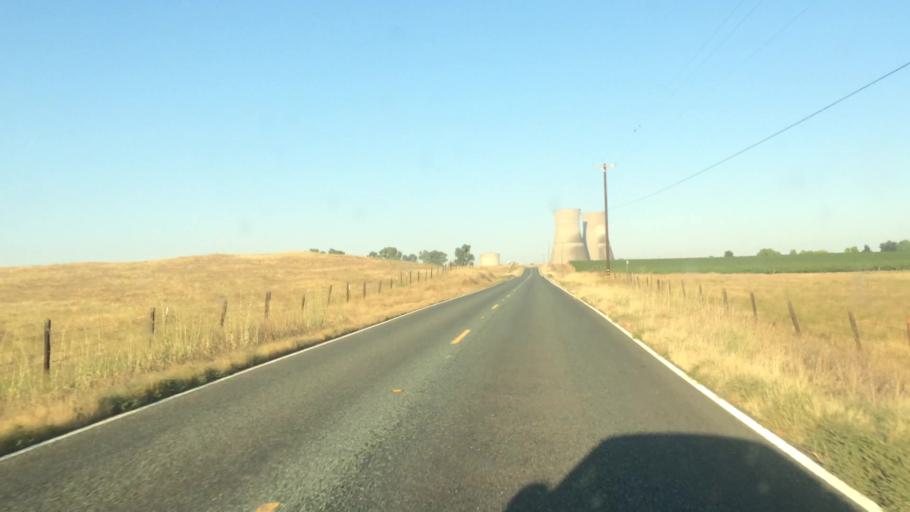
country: US
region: California
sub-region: Sacramento County
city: Clay
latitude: 38.3479
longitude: -121.1016
